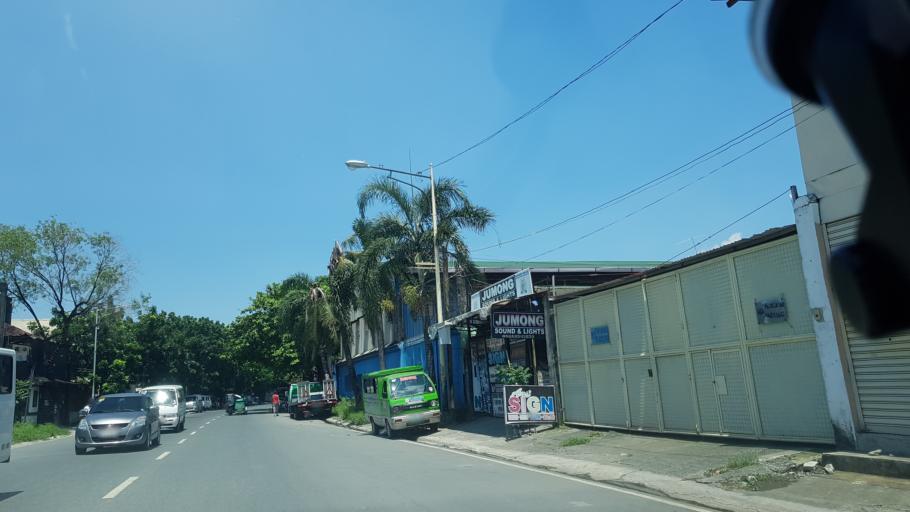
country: PH
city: Sambayanihan People's Village
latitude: 14.4669
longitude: 120.9964
